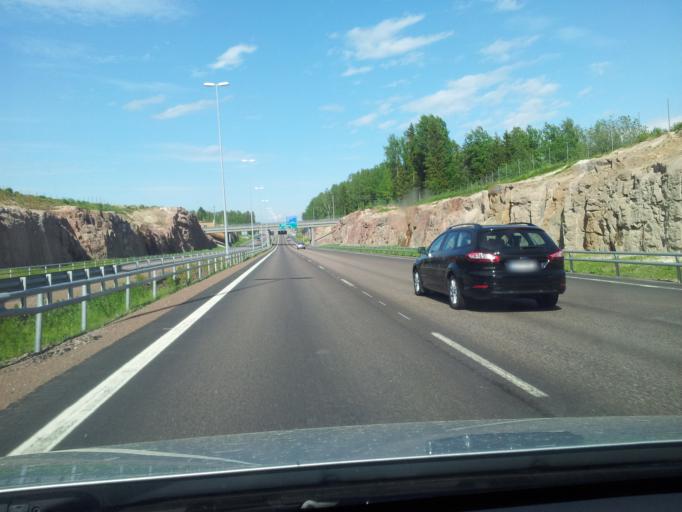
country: FI
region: Kymenlaakso
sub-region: Kotka-Hamina
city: Hamina
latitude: 60.5895
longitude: 27.1594
